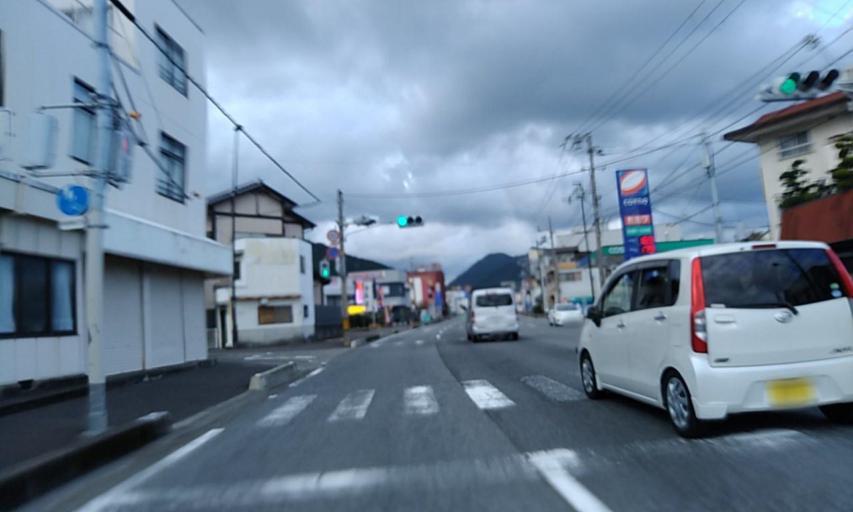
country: JP
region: Wakayama
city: Shingu
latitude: 33.7171
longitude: 135.9874
